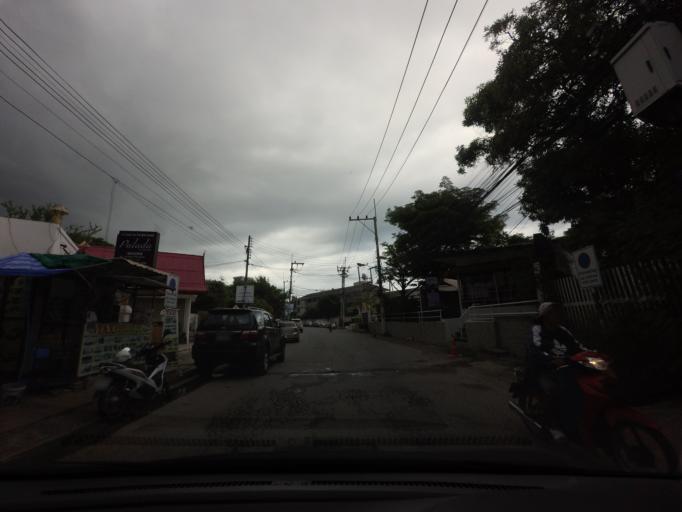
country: TH
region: Prachuap Khiri Khan
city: Hua Hin
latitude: 12.5659
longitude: 99.9598
